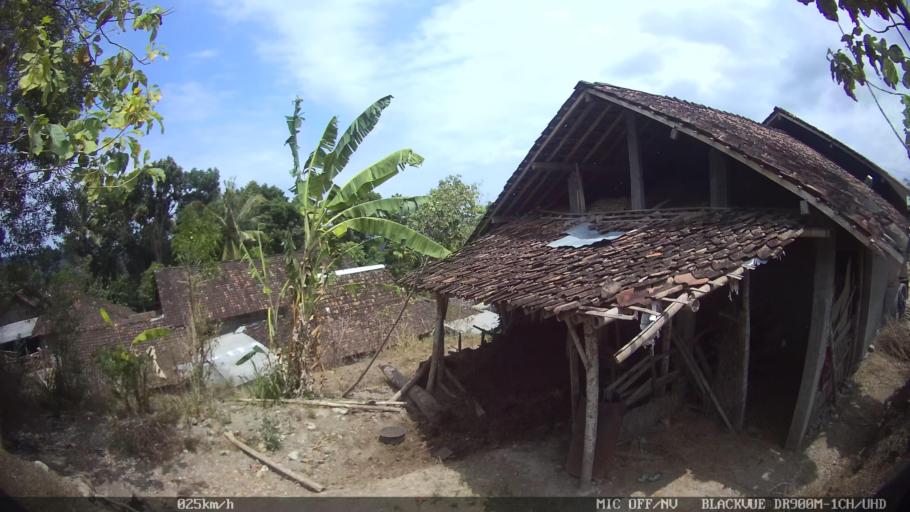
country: ID
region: Central Java
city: Candi Prambanan
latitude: -7.8120
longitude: 110.5241
